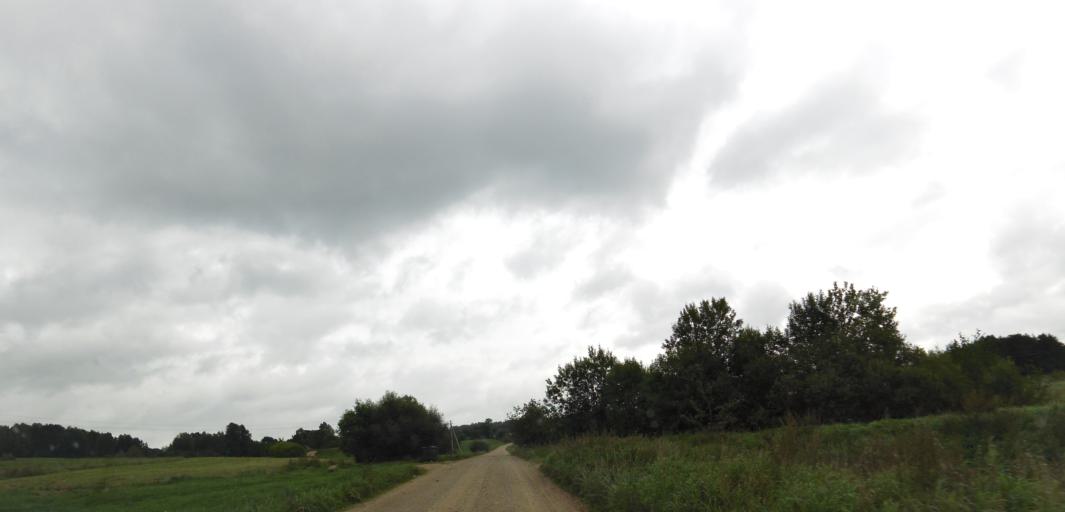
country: LT
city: Moletai
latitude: 55.3455
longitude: 25.3809
